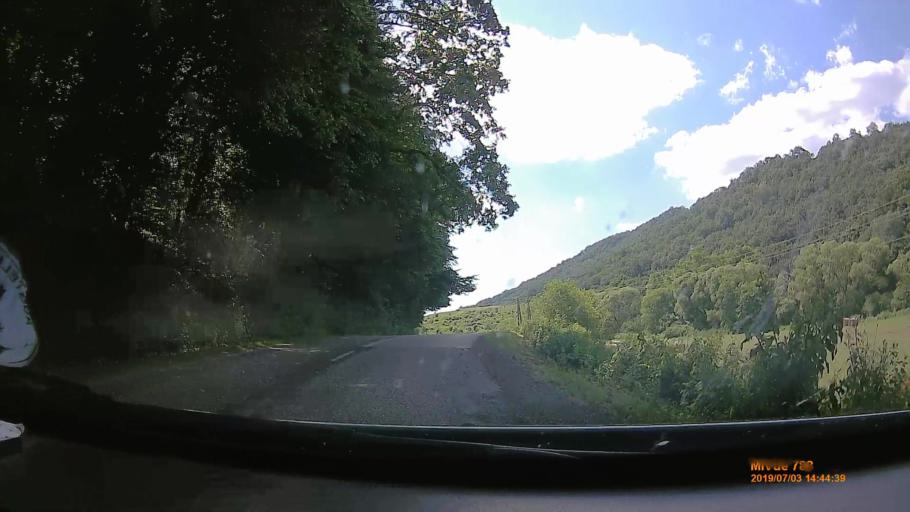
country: HU
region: Borsod-Abauj-Zemplen
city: Putnok
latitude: 48.2643
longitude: 20.4290
